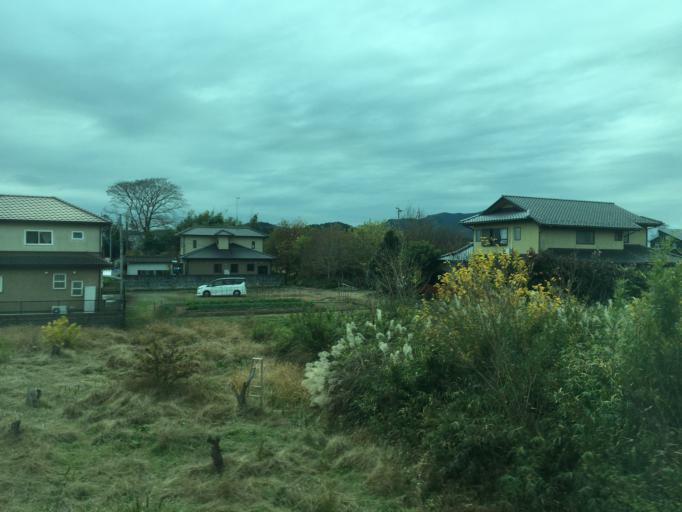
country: JP
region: Ibaraki
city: Tomobe
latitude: 36.3460
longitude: 140.2863
